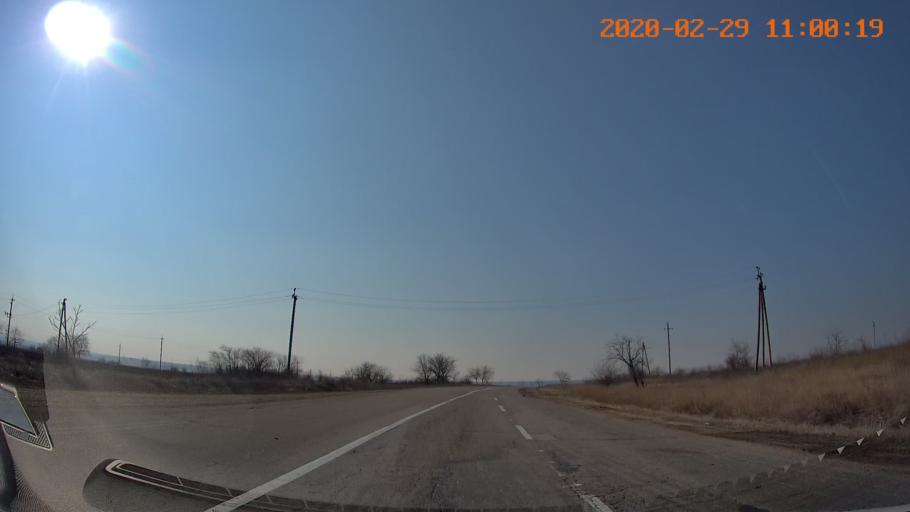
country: MD
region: Telenesti
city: Grigoriopol
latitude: 47.1628
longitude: 29.2792
